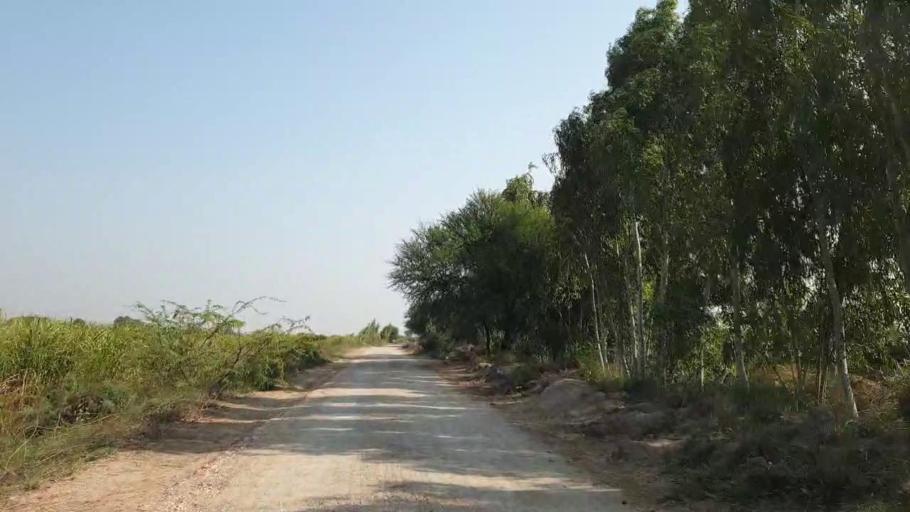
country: PK
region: Sindh
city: Bulri
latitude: 24.9314
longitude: 68.3736
